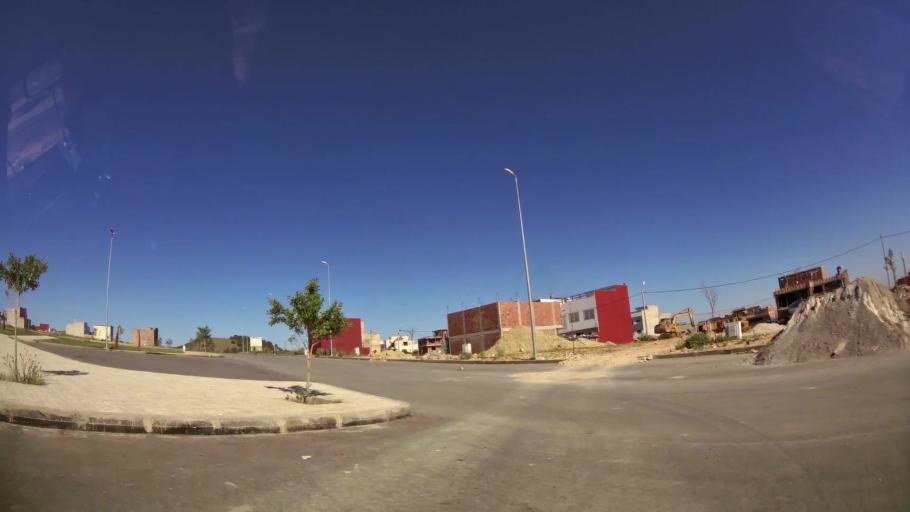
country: MA
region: Oriental
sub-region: Oujda-Angad
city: Oujda
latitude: 34.6450
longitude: -1.8870
